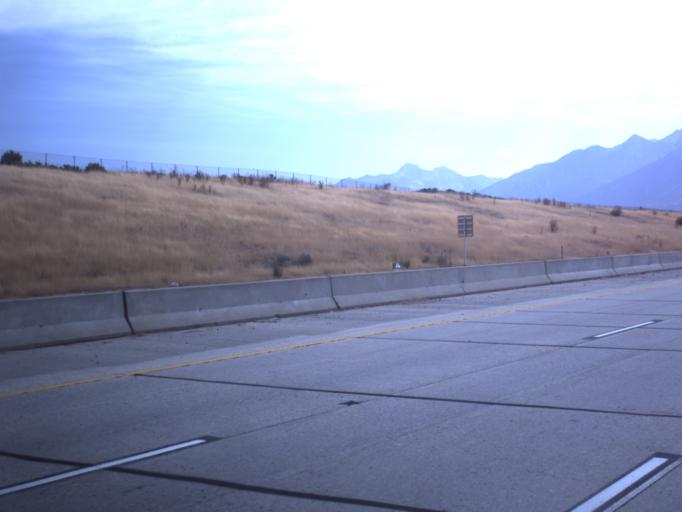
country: US
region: Utah
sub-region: Salt Lake County
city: Bluffdale
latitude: 40.4967
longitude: -111.9184
